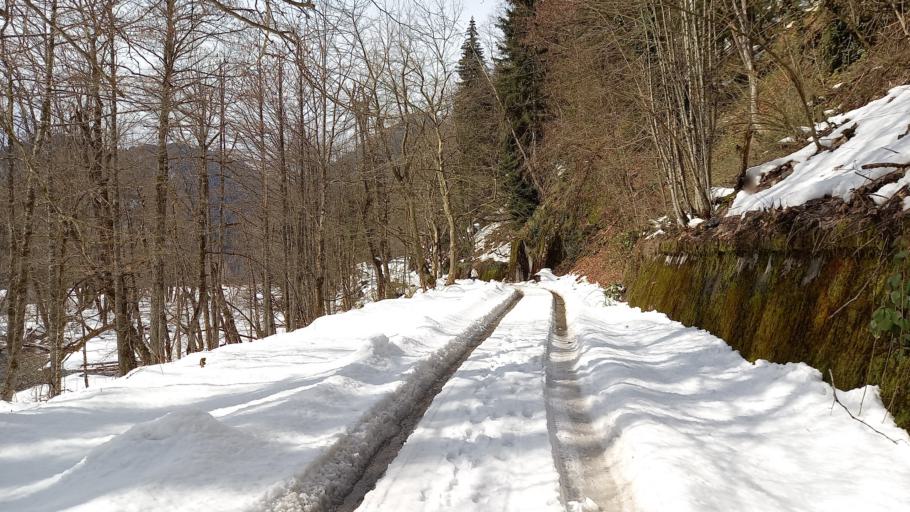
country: GE
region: Abkhazia
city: Gagra
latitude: 43.4821
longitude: 40.5618
